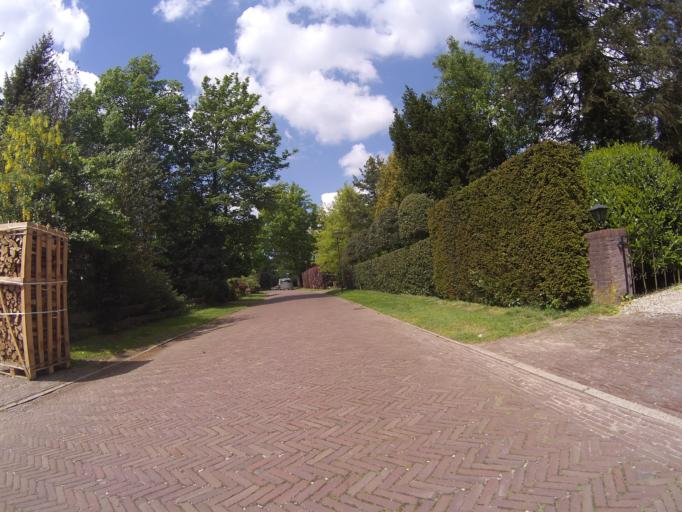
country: NL
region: North Holland
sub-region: Gemeente Laren
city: Laren
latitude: 52.2674
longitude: 5.2301
